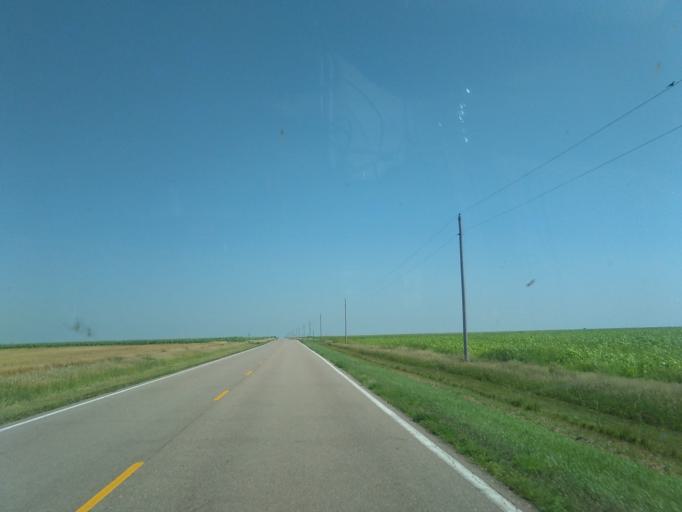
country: US
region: Nebraska
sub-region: Dundy County
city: Benkelman
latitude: 39.8277
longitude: -101.5411
